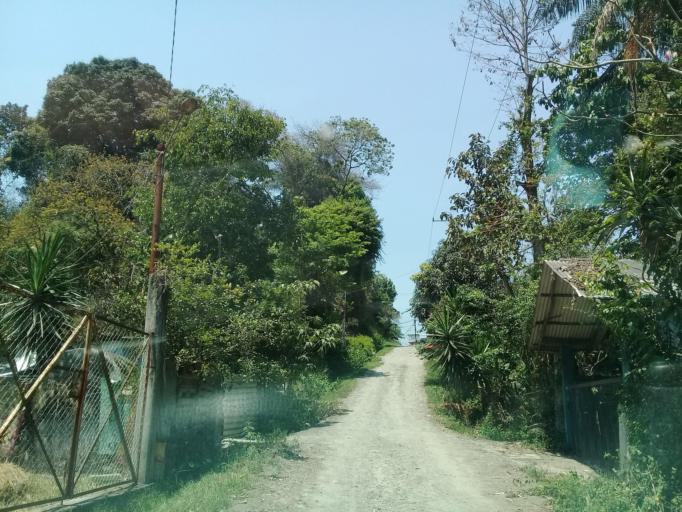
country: MX
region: Veracruz
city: Paraje Nuevo
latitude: 18.8722
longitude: -96.8653
